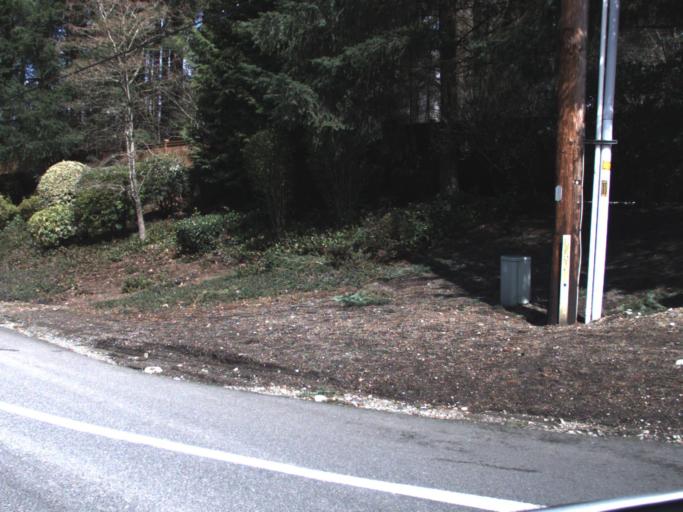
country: US
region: Washington
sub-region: King County
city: Maple Valley
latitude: 47.3750
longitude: -122.0249
